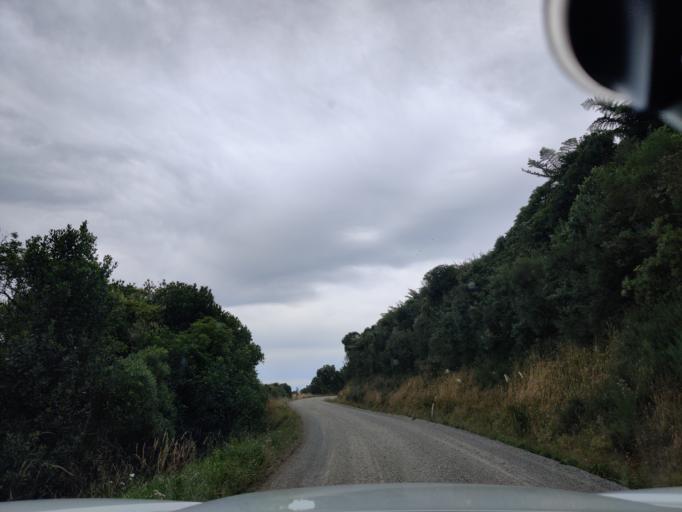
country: NZ
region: Wellington
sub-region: Masterton District
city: Masterton
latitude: -41.0382
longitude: 175.4154
